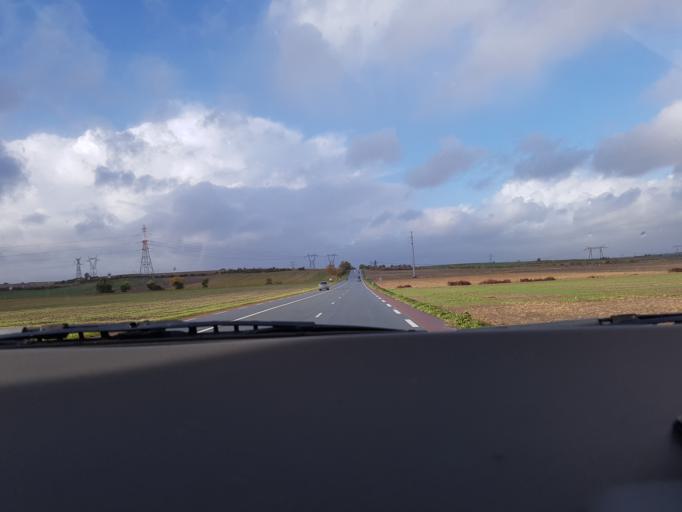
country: FR
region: Poitou-Charentes
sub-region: Departement de la Charente-Maritime
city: Les Gonds
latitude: 45.6660
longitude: -0.5969
